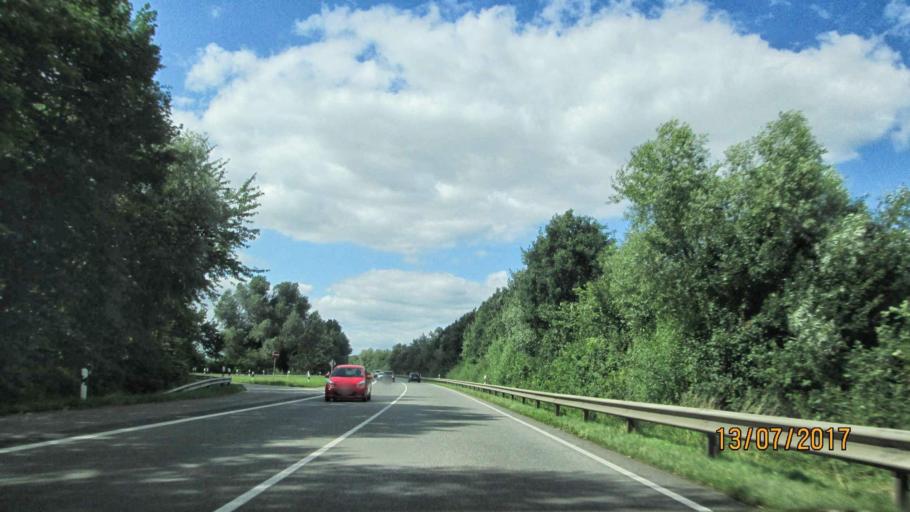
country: DE
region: Lower Saxony
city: Handorf
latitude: 53.3785
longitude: 10.3482
